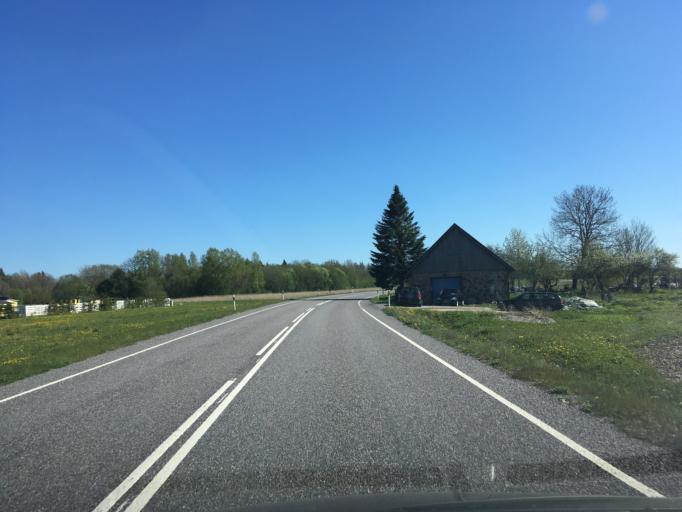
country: EE
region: Harju
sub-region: Rae vald
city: Vaida
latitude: 59.2642
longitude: 25.0211
